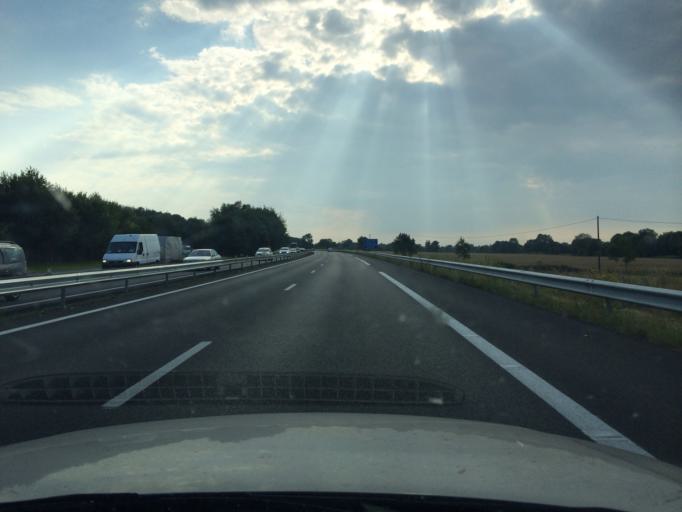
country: FR
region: Lower Normandy
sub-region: Departement du Calvados
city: Touques
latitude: 49.2572
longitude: 0.0904
